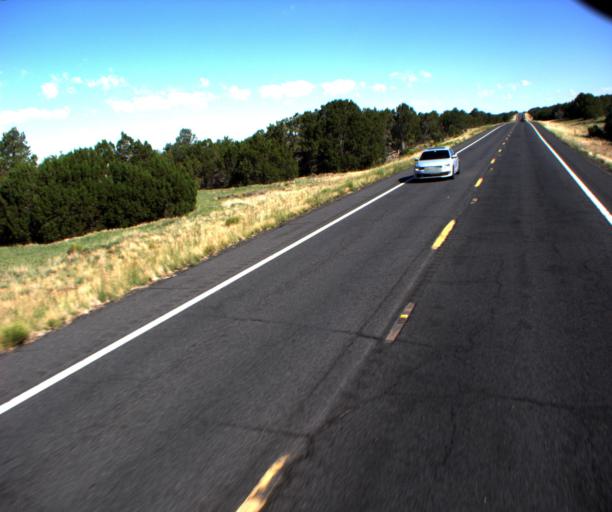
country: US
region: Arizona
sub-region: Coconino County
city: Williams
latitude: 35.3872
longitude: -112.1646
